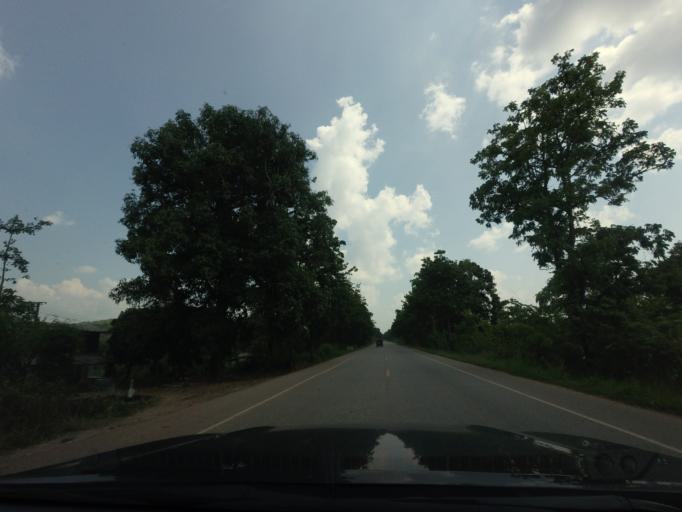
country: TH
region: Phitsanulok
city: Chat Trakan
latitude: 17.2773
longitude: 100.5396
